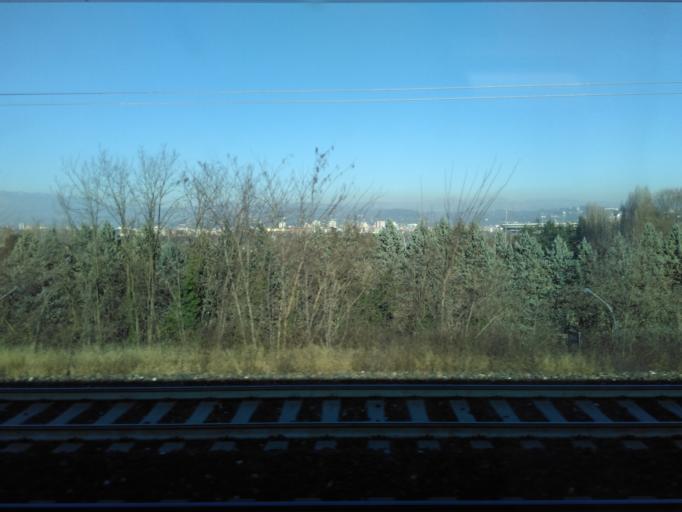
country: IT
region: Veneto
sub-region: Provincia di Verona
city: Verona
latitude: 45.4269
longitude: 10.9609
